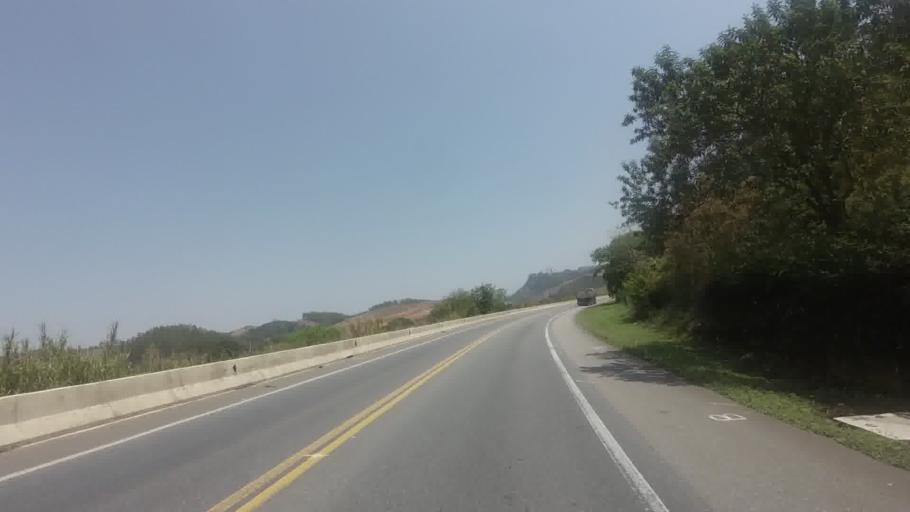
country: BR
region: Espirito Santo
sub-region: Rio Novo Do Sul
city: Rio Novo do Sul
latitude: -20.8760
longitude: -40.9544
